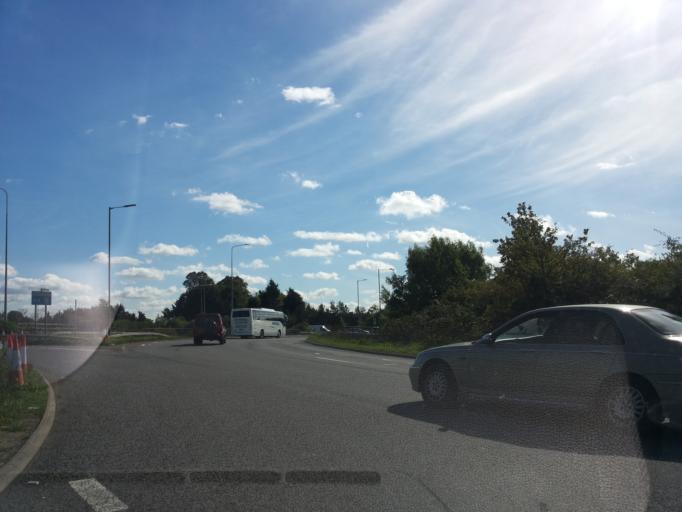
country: GB
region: England
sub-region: Kent
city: Boxley
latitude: 51.2886
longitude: 0.5523
